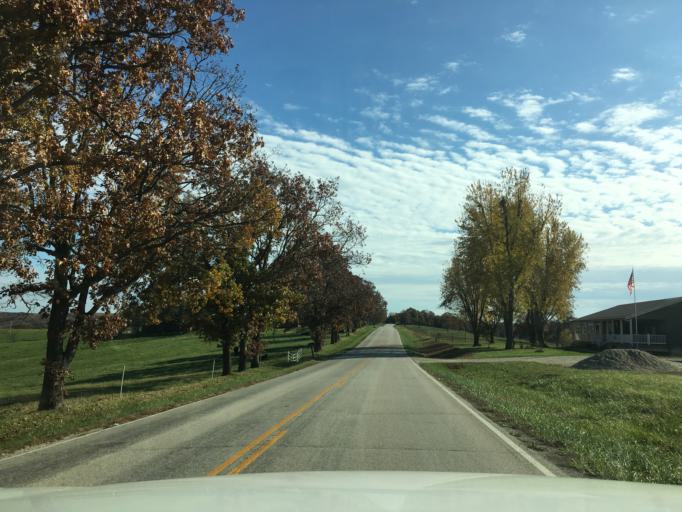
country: US
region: Missouri
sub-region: Maries County
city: Belle
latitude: 38.3512
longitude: -91.7981
